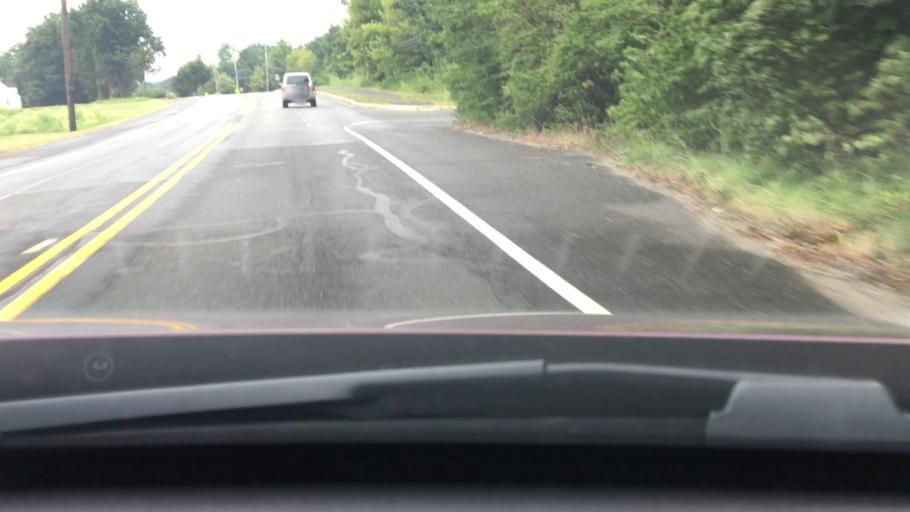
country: US
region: Maryland
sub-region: Prince George's County
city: Calverton
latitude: 39.0574
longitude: -76.9221
